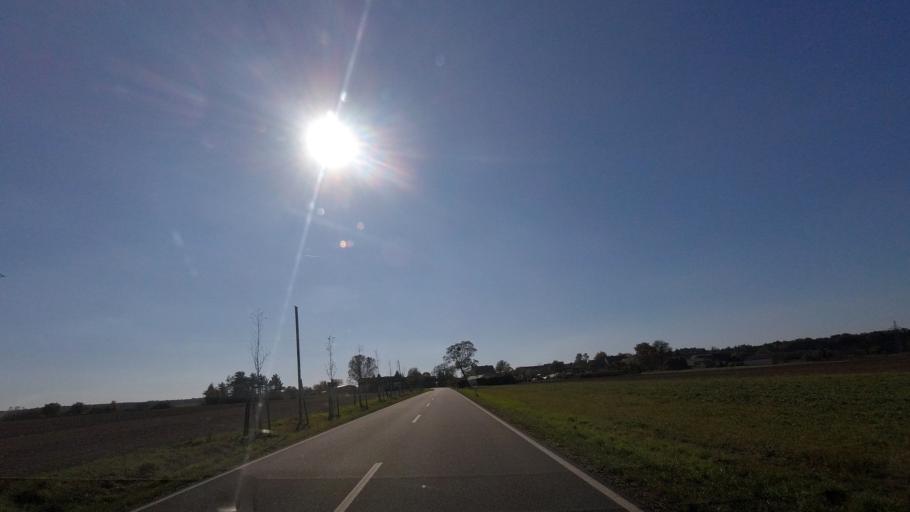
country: DE
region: Saxony-Anhalt
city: Muhlanger
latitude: 51.8693
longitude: 12.7854
